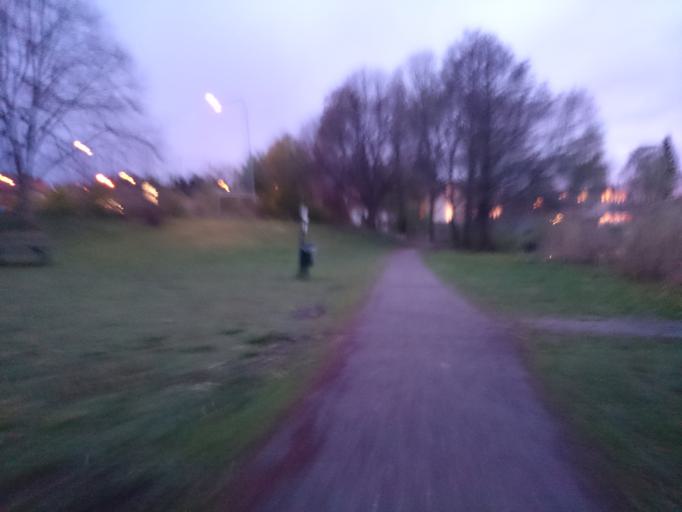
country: SE
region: Stockholm
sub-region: Huddinge Kommun
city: Huddinge
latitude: 59.2665
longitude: 17.9660
